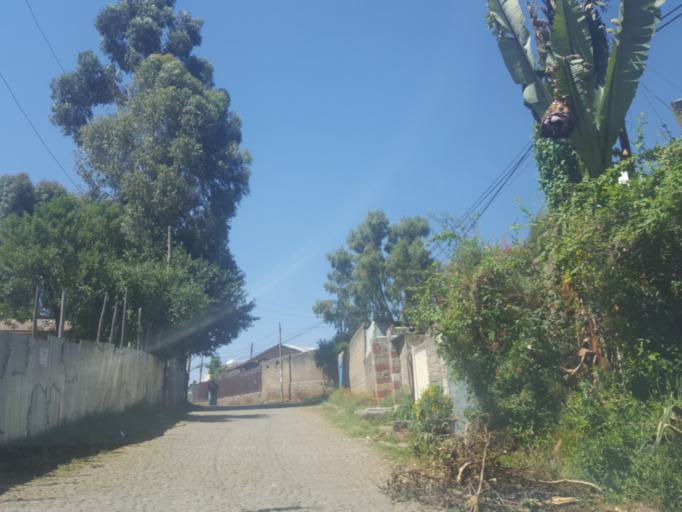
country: ET
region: Adis Abeba
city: Addis Ababa
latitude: 9.0621
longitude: 38.7394
